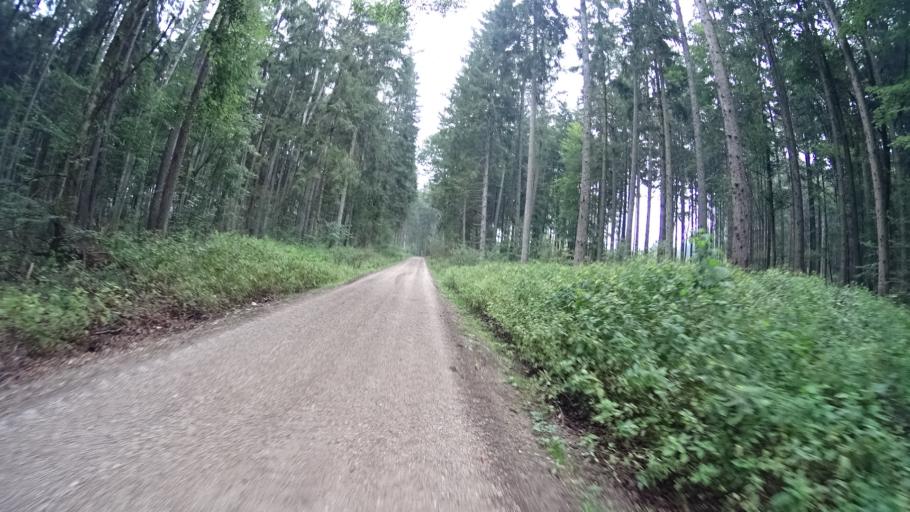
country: DE
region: Bavaria
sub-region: Upper Bavaria
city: Stammham
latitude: 48.8559
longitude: 11.4947
